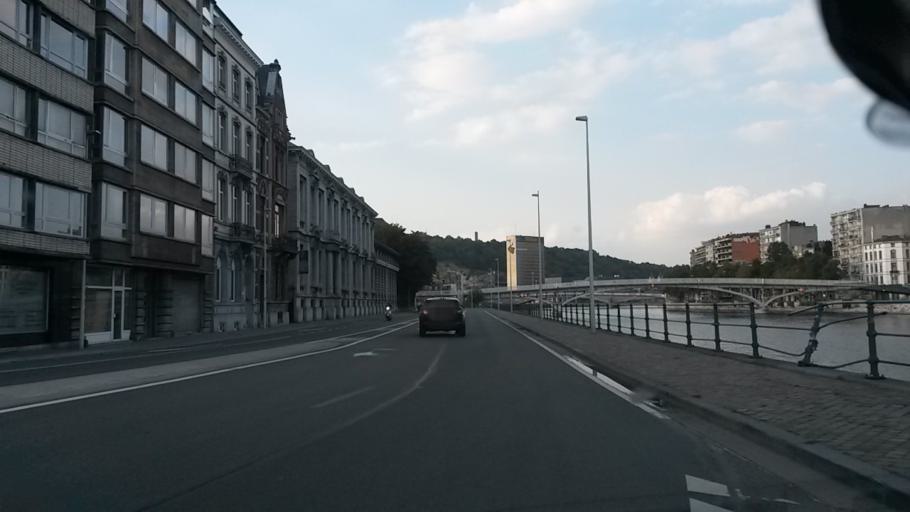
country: BE
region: Wallonia
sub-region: Province de Liege
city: Liege
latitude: 50.6394
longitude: 5.5768
